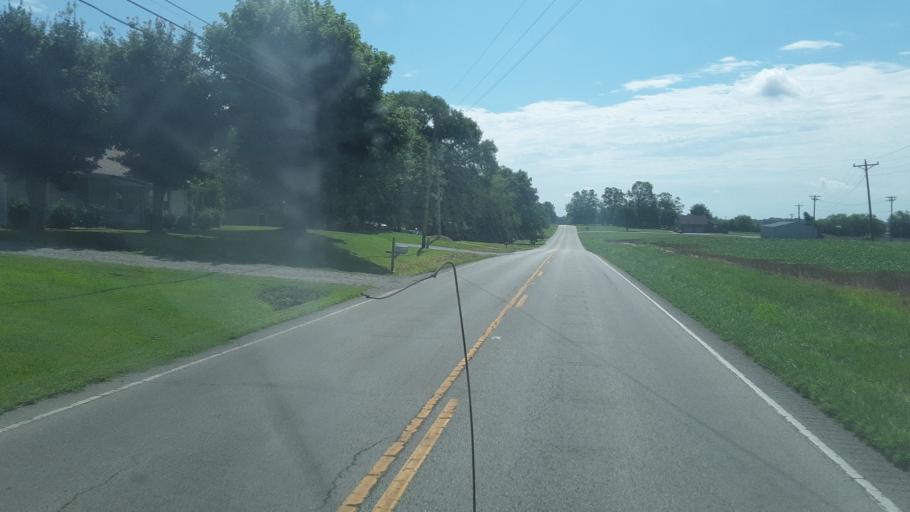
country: US
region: Kentucky
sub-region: Todd County
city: Elkton
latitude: 36.8170
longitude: -87.1855
